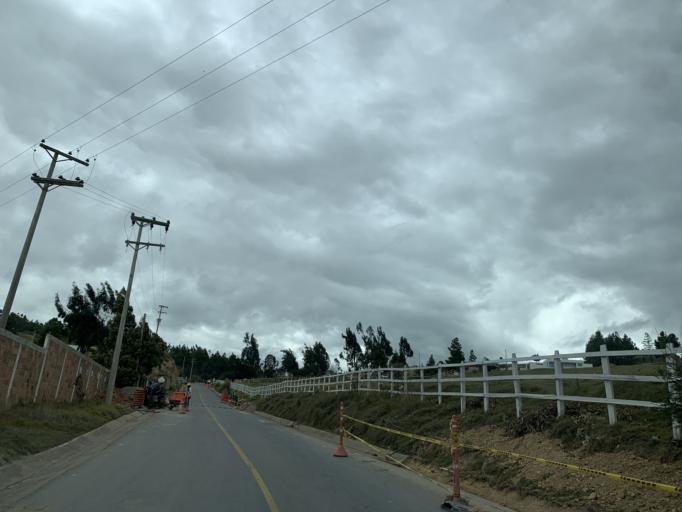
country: CO
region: Boyaca
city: Tunja
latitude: 5.5305
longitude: -73.3378
